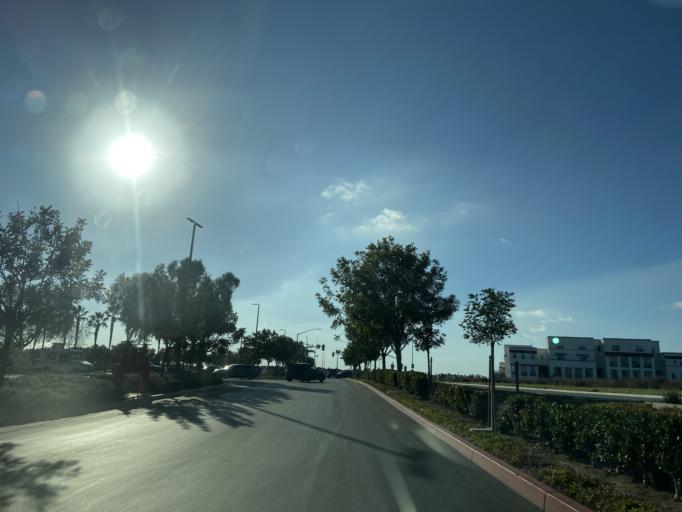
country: US
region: California
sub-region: San Diego County
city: Bonita
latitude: 32.6264
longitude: -116.9669
